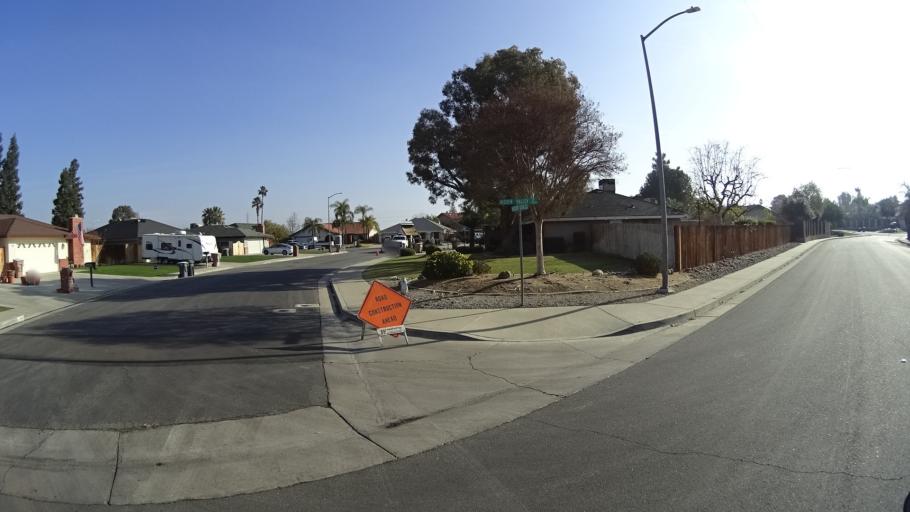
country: US
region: California
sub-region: Kern County
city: Oildale
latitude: 35.4059
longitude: -118.9290
